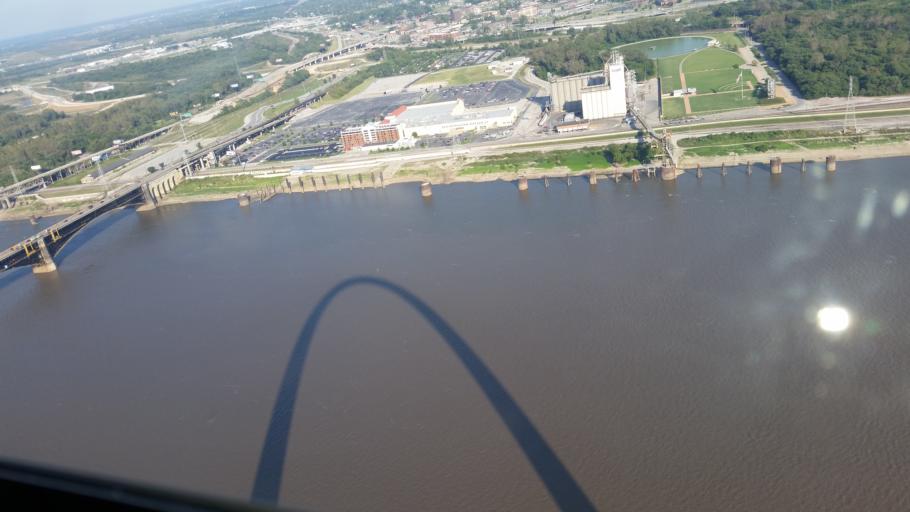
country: US
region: Missouri
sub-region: City of Saint Louis
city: St. Louis
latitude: 38.6249
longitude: -90.1844
